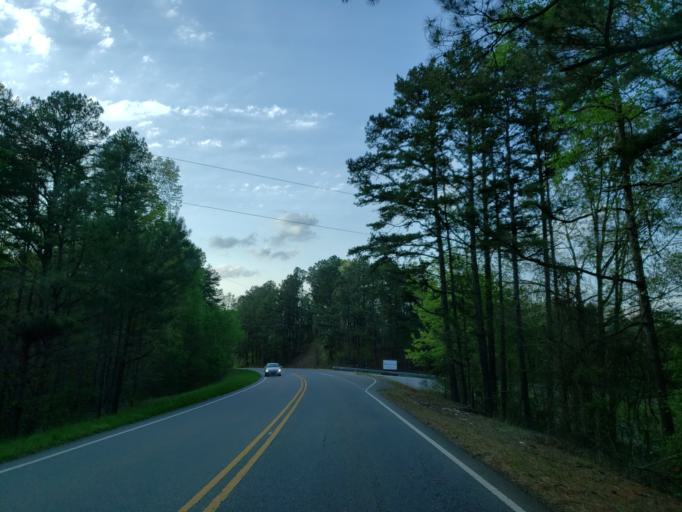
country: US
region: Georgia
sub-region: Cherokee County
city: Ball Ground
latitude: 34.2753
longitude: -84.3723
